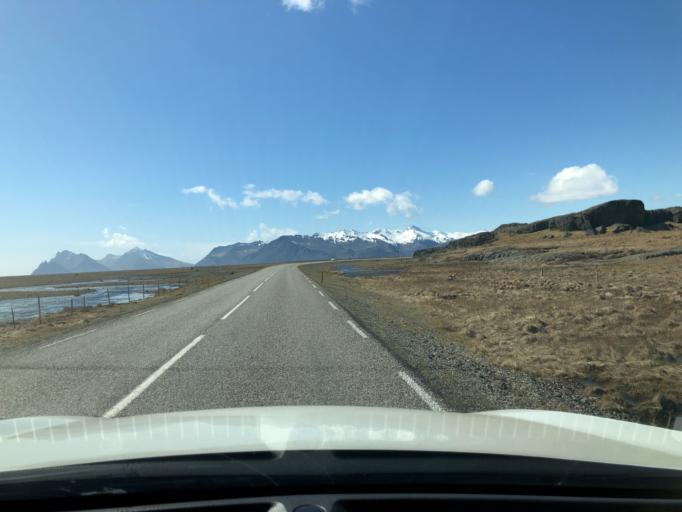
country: IS
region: East
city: Hoefn
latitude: 64.4193
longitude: -14.7257
